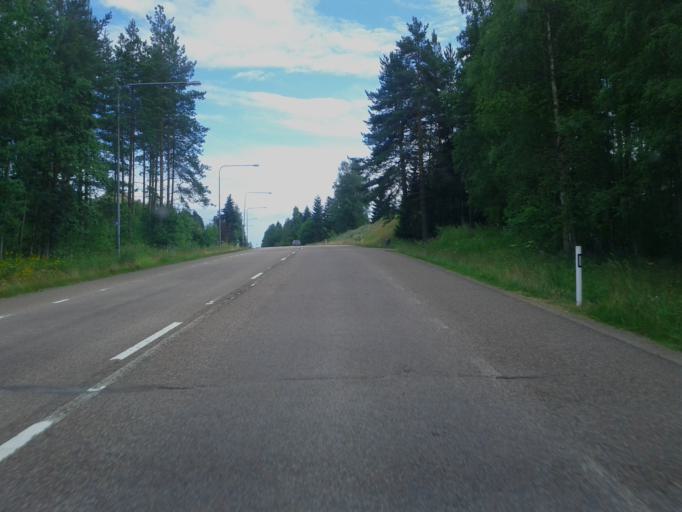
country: SE
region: Dalarna
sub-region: Faluns Kommun
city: Bjursas
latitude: 60.7311
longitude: 15.4409
